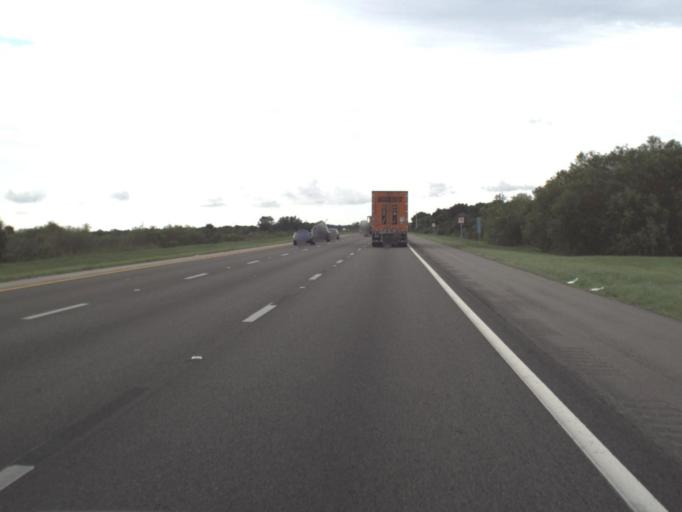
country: US
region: Florida
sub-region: Sarasota County
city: Laurel
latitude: 27.1887
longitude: -82.4386
